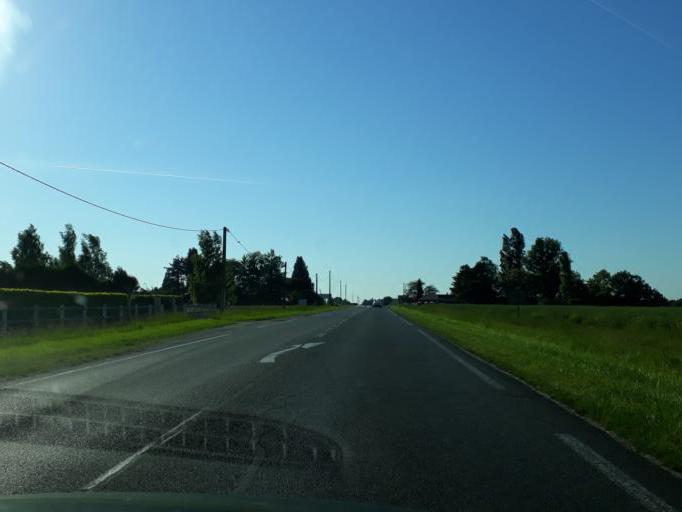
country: FR
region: Centre
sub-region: Departement du Loiret
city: Bonny-sur-Loire
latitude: 47.5877
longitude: 2.8076
